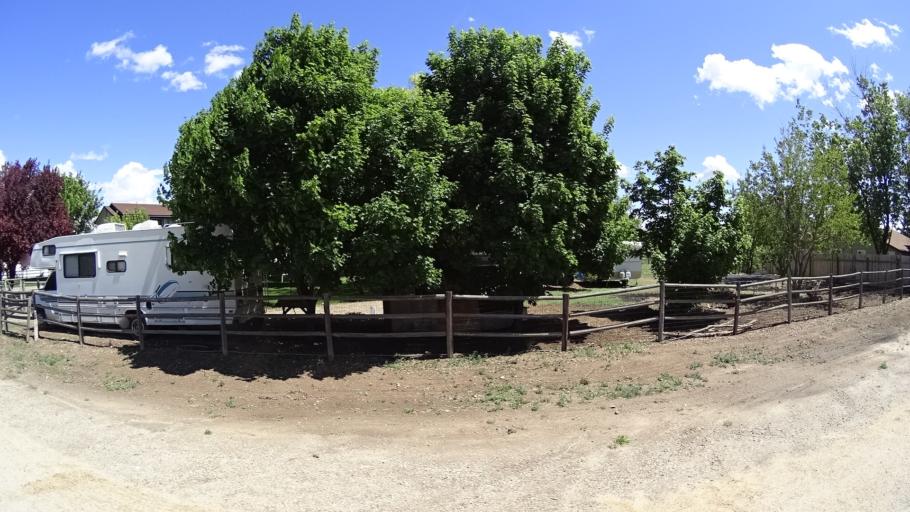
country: US
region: Idaho
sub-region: Ada County
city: Meridian
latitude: 43.5916
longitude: -116.4735
